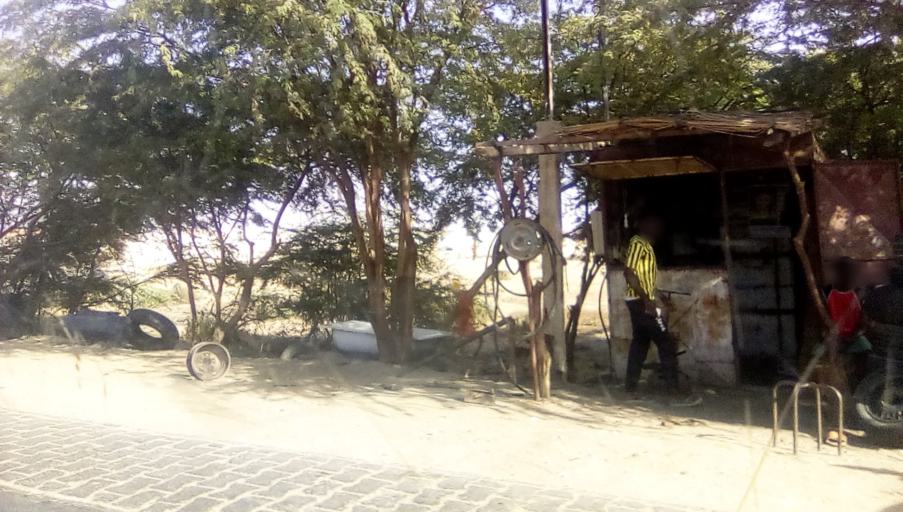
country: SN
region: Saint-Louis
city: Saint-Louis
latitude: 16.0384
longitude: -16.4574
